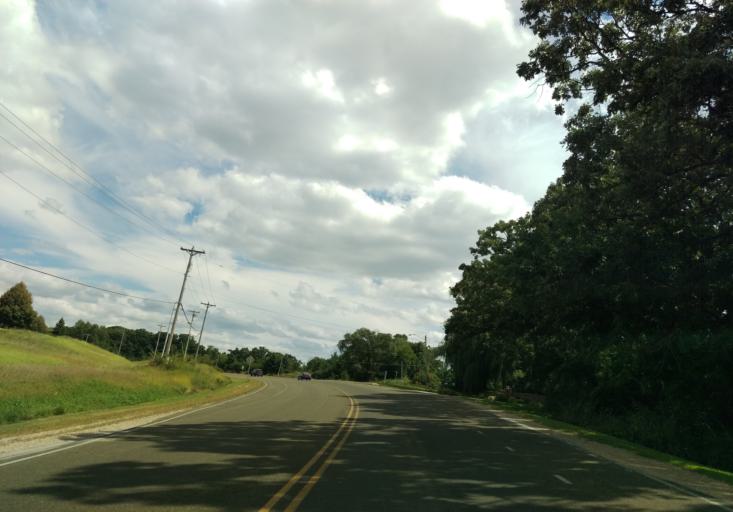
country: US
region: Wisconsin
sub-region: Dane County
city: Shorewood Hills
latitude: 43.1119
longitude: -89.4605
